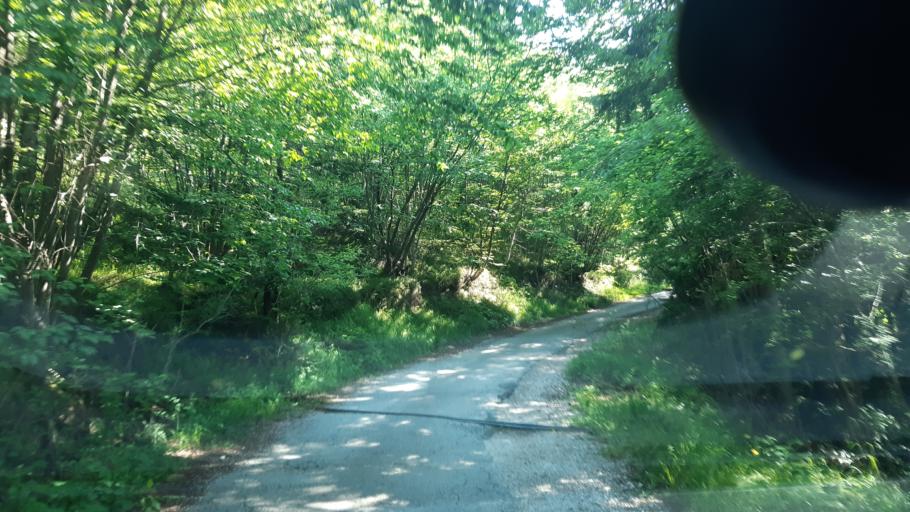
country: SI
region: Trzic
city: Bistrica pri Trzicu
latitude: 46.3603
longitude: 14.2764
